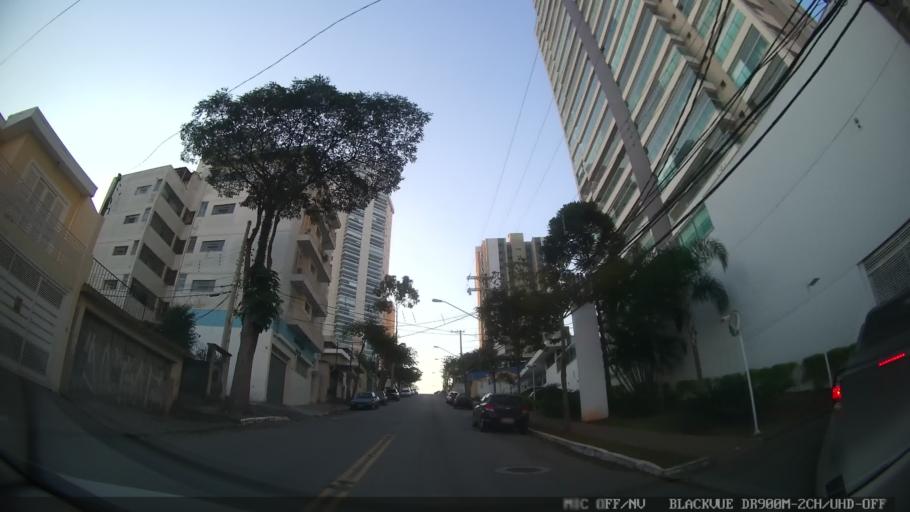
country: BR
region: Sao Paulo
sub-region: Sao Paulo
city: Sao Paulo
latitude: -23.5001
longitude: -46.6412
